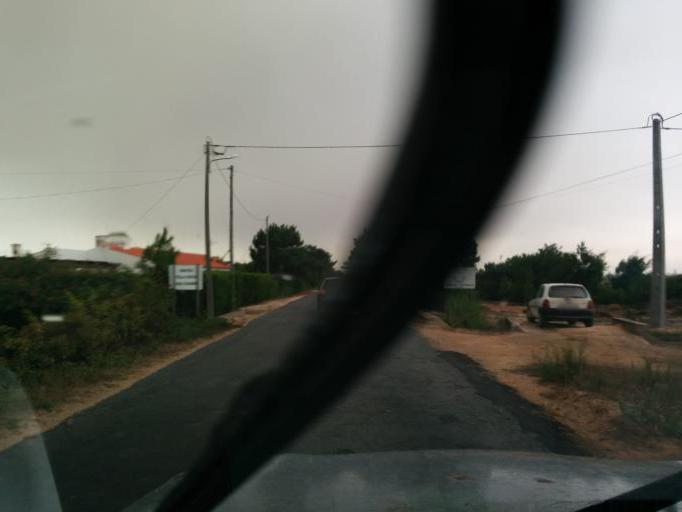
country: PT
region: Beja
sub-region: Odemira
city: Vila Nova de Milfontes
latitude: 37.6145
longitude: -8.7899
